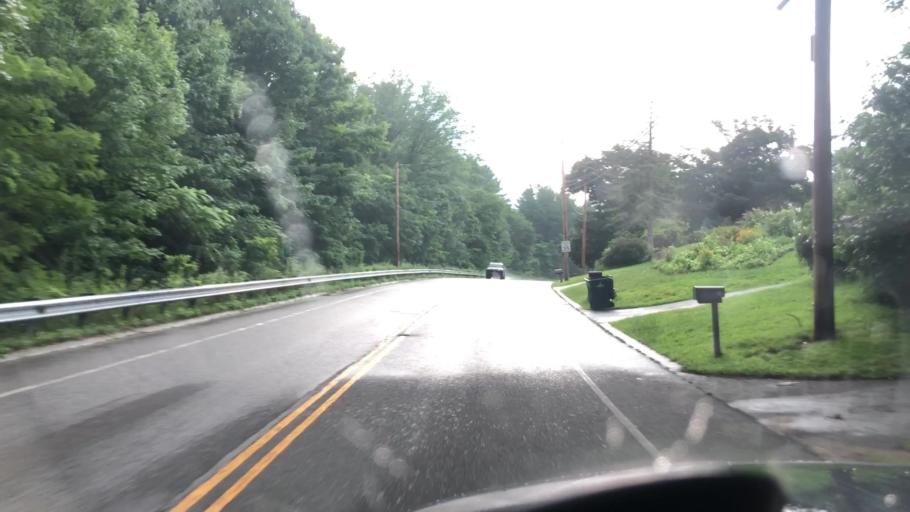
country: US
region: Massachusetts
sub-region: Hampshire County
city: Easthampton
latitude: 42.3009
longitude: -72.6777
